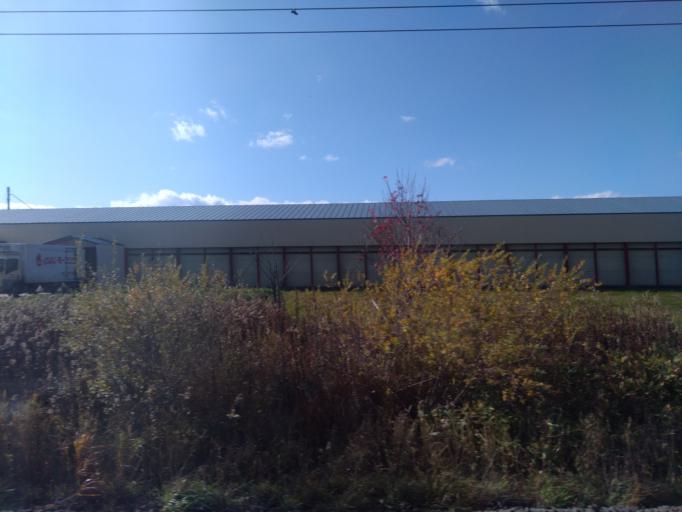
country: JP
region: Hokkaido
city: Kitahiroshima
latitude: 42.9567
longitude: 141.5696
